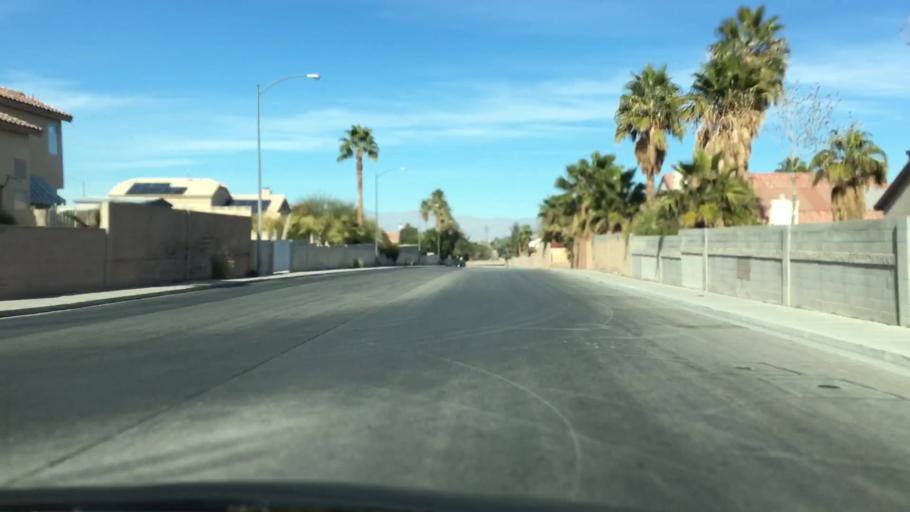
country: US
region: Nevada
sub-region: Clark County
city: Paradise
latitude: 36.0386
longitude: -115.1407
